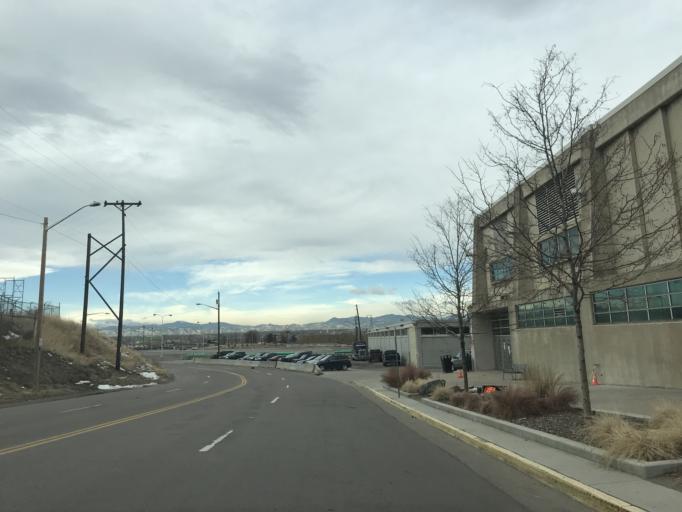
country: US
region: Colorado
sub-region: Denver County
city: Denver
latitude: 39.7787
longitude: -104.9708
